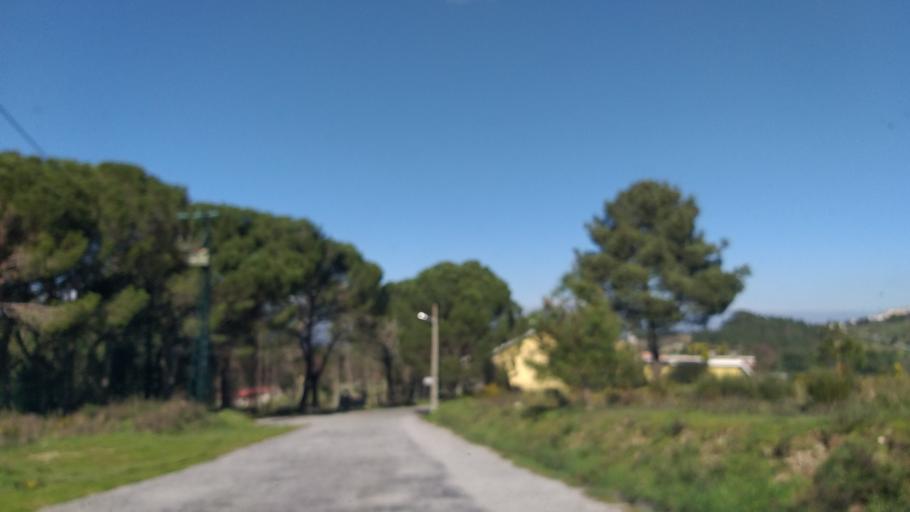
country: PT
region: Guarda
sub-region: Seia
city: Seia
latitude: 40.4731
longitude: -7.6245
